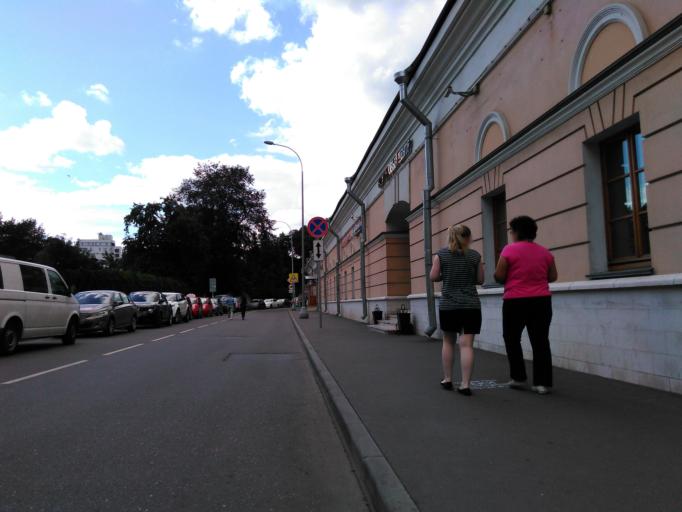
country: RU
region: Moskovskaya
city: Dorogomilovo
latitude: 55.7289
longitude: 37.5805
